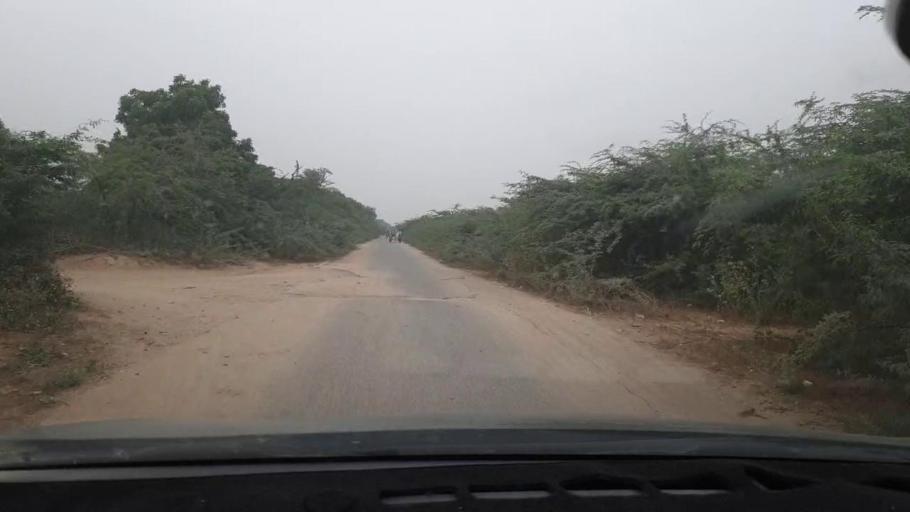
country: PK
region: Sindh
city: Malir Cantonment
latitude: 24.9256
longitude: 67.3246
